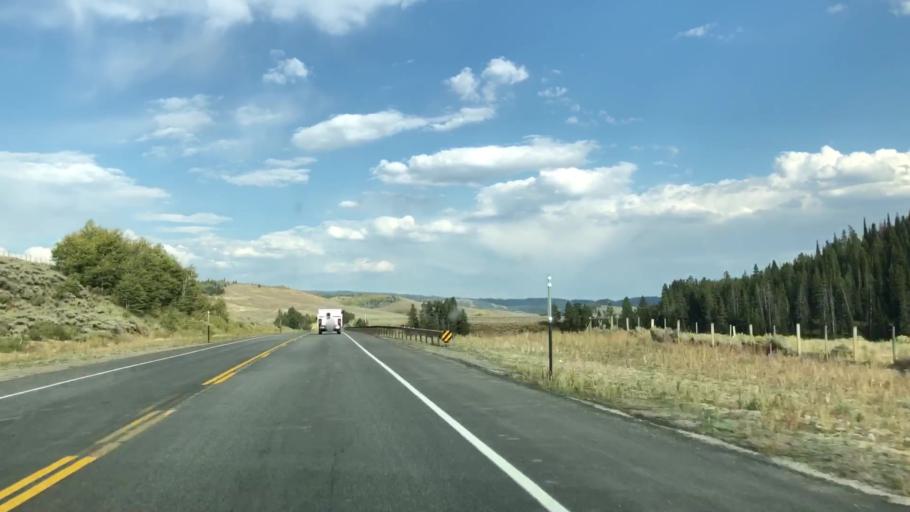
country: US
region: Wyoming
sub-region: Teton County
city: Hoback
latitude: 43.1564
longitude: -110.3137
